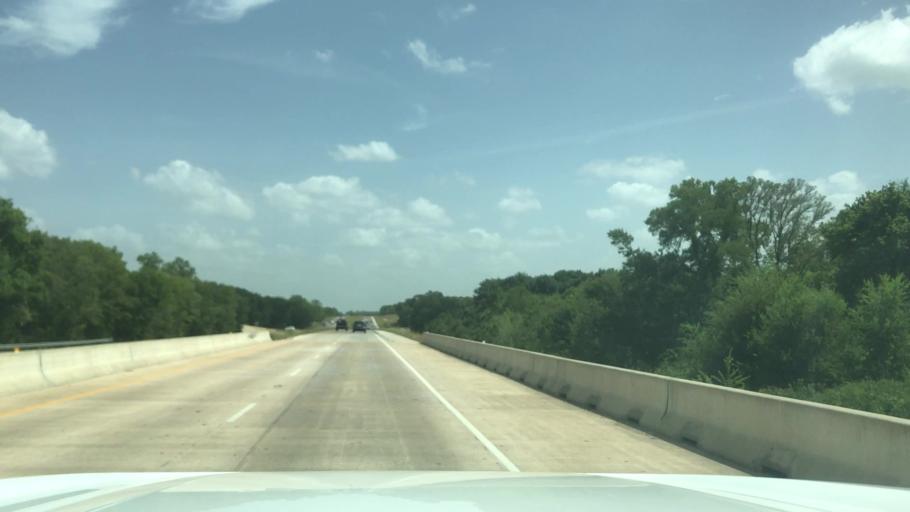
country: US
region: Texas
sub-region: Robertson County
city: Calvert
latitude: 30.9470
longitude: -96.6478
